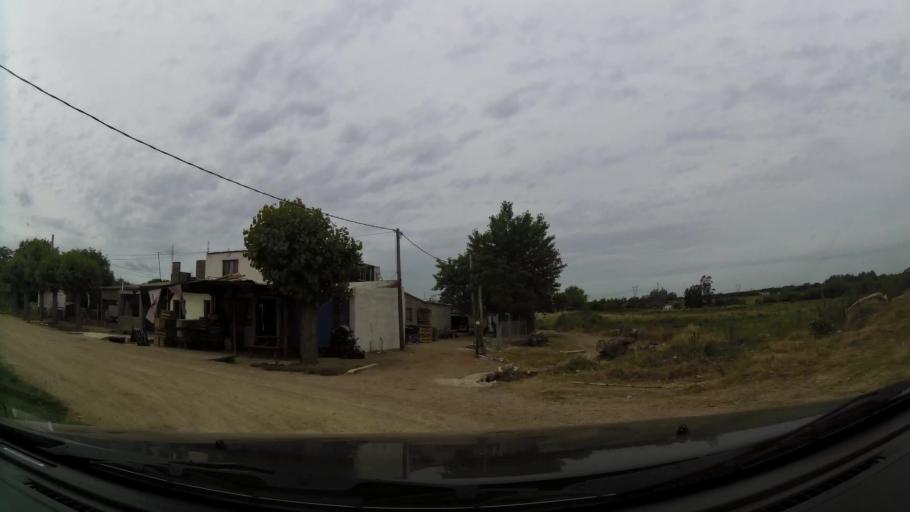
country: UY
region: Canelones
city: Las Piedras
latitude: -34.7202
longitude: -56.1902
